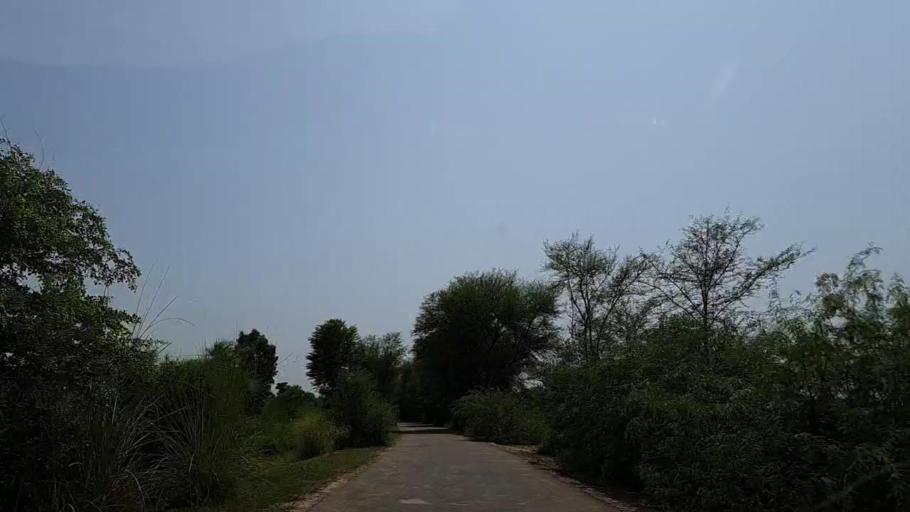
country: PK
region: Sindh
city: Adilpur
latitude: 27.9109
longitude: 69.3657
